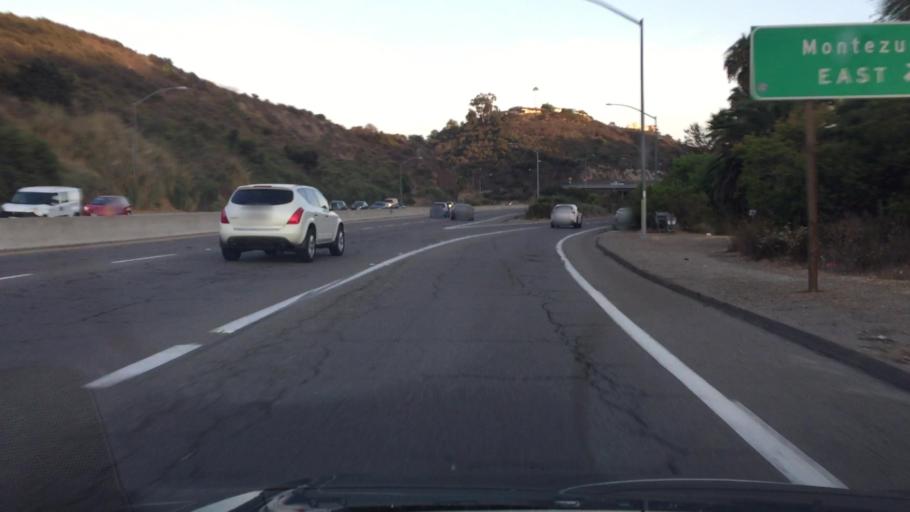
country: US
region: California
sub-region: San Diego County
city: Lemon Grove
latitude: 32.7754
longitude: -117.0988
